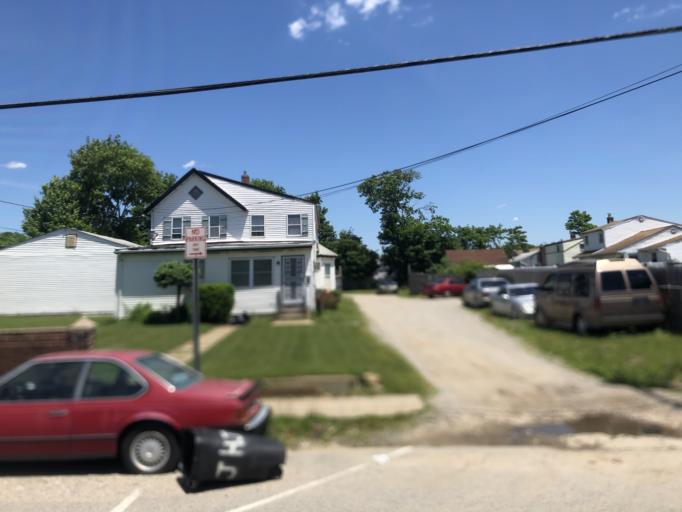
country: US
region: New York
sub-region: Nassau County
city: Freeport
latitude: 40.6693
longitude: -73.5769
